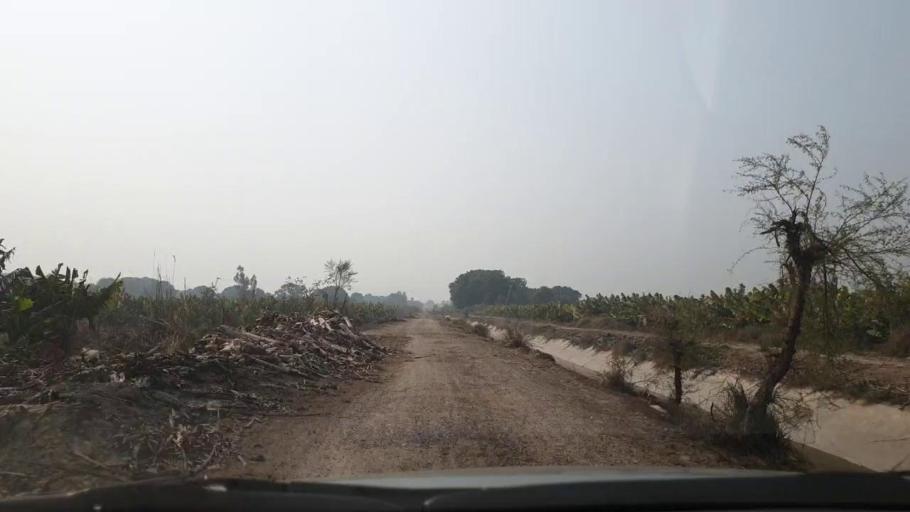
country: PK
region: Sindh
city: Matiari
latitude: 25.6355
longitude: 68.5084
